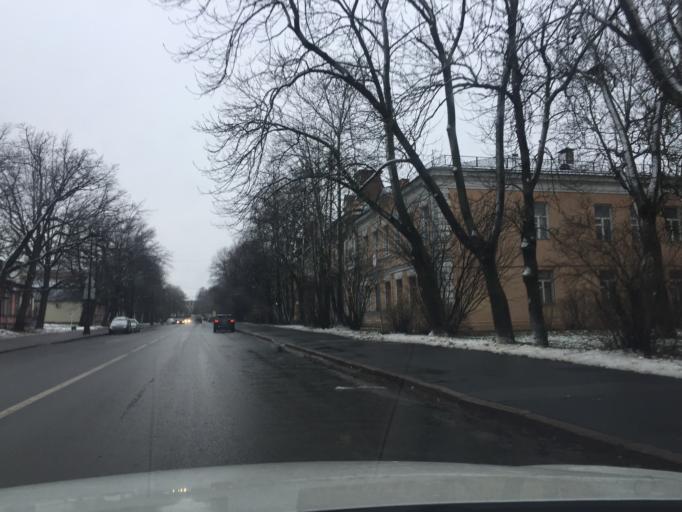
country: RU
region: St.-Petersburg
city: Pushkin
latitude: 59.7219
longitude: 30.4060
